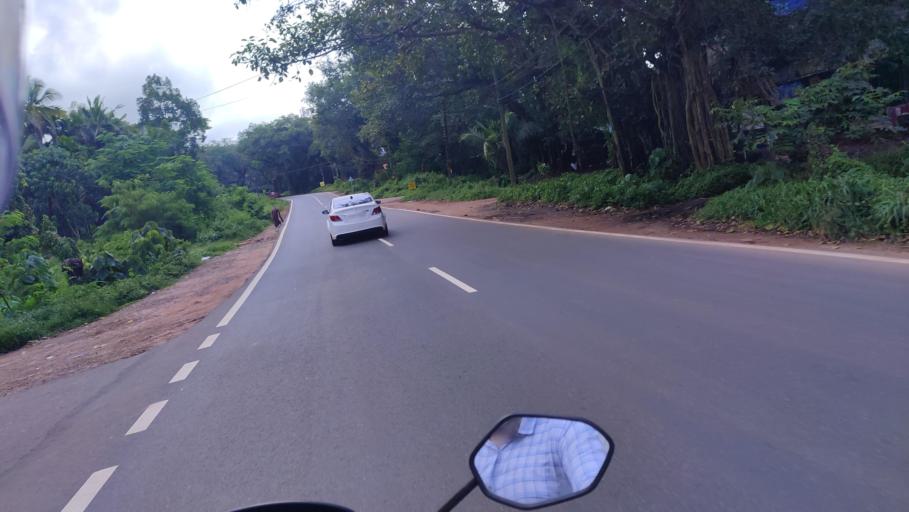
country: IN
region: Kerala
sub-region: Kasaragod District
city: Nileshwar
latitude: 12.2261
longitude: 75.1577
